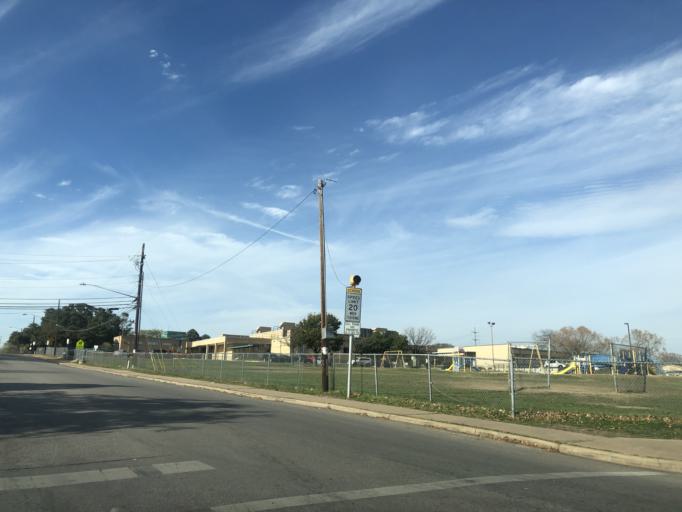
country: US
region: Texas
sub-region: Travis County
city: Onion Creek
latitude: 30.1807
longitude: -97.7625
